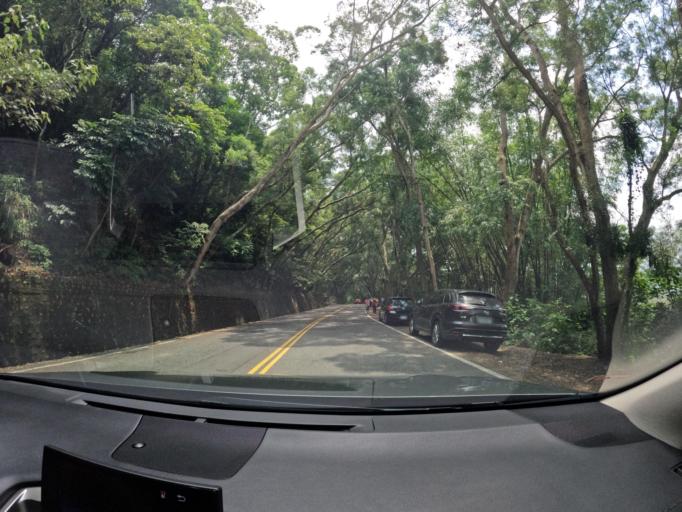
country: TW
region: Taiwan
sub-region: Nantou
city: Nantou
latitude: 23.8889
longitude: 120.6271
